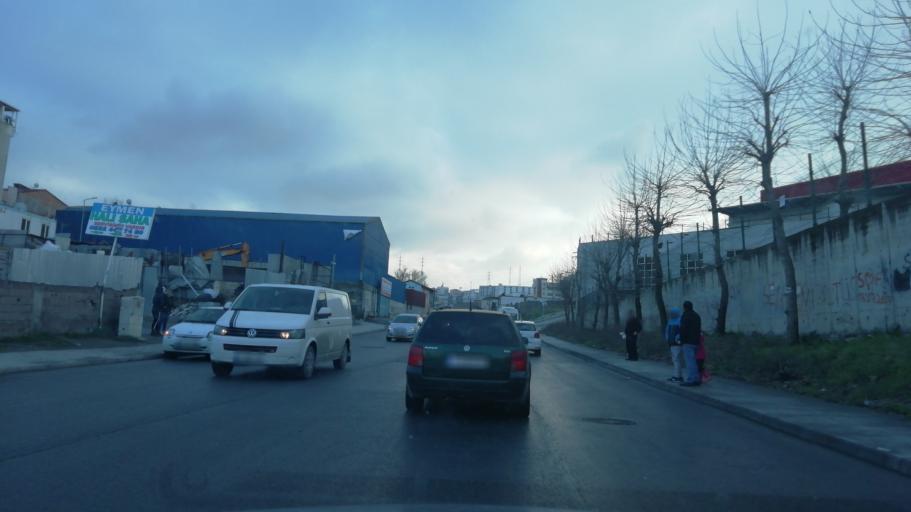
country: TR
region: Istanbul
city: Esenyurt
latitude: 41.0283
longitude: 28.7018
